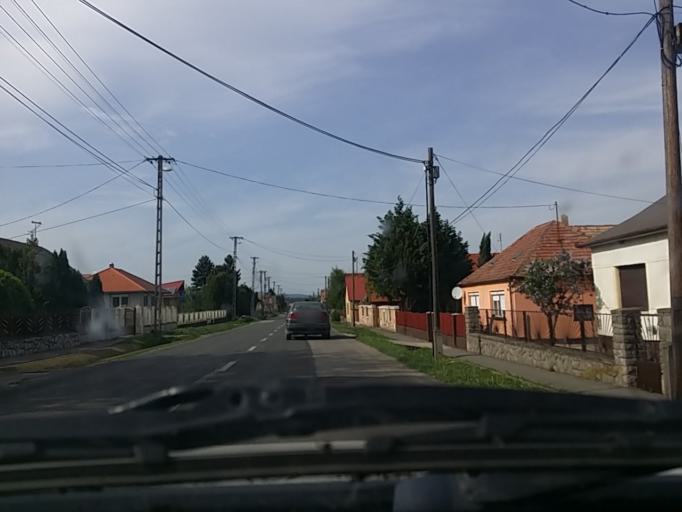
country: HU
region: Baranya
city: Harkany
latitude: 45.9446
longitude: 18.2378
